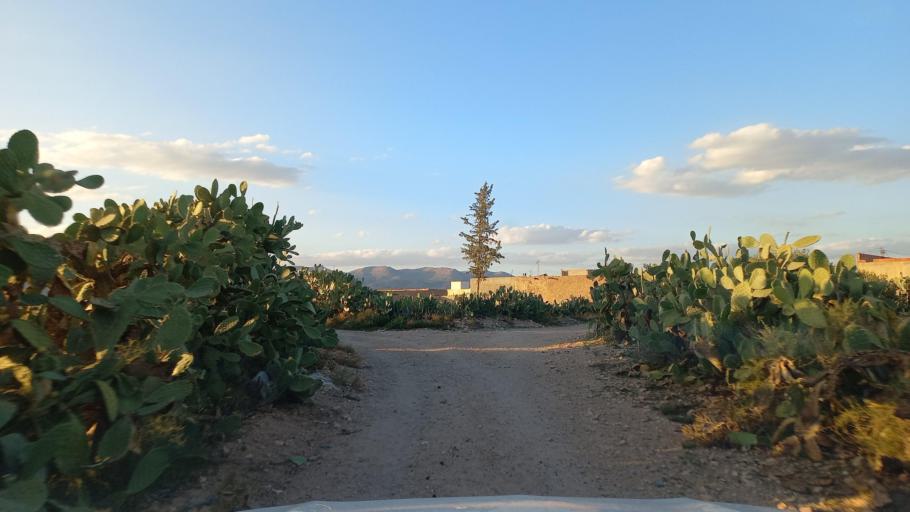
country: TN
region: Al Qasrayn
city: Sbiba
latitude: 35.3749
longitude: 9.0554
